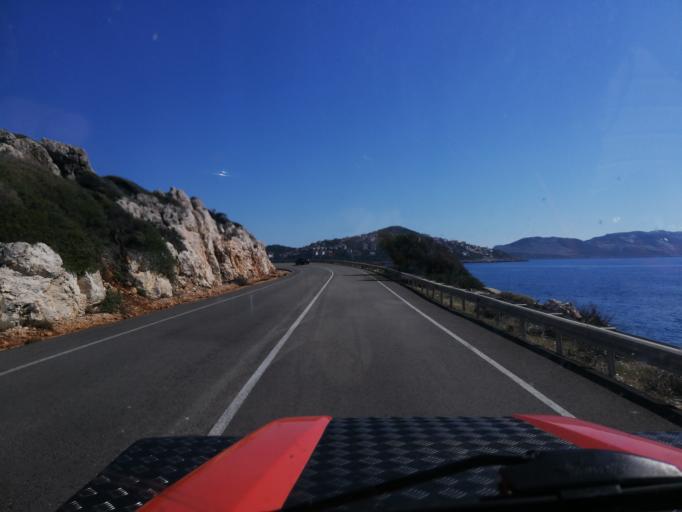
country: GR
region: South Aegean
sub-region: Nomos Dodekanisou
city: Megisti
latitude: 36.2028
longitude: 29.5792
